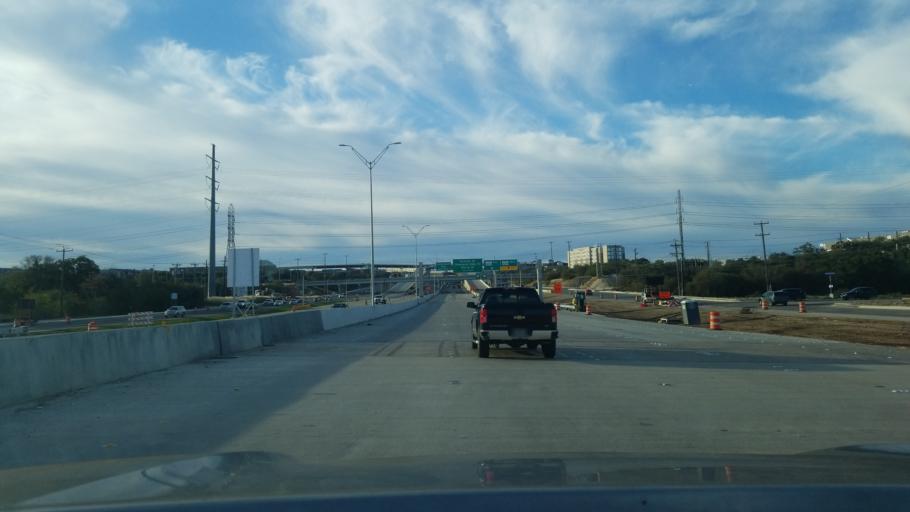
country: US
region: Texas
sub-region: Bexar County
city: Hollywood Park
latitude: 29.6178
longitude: -98.4652
